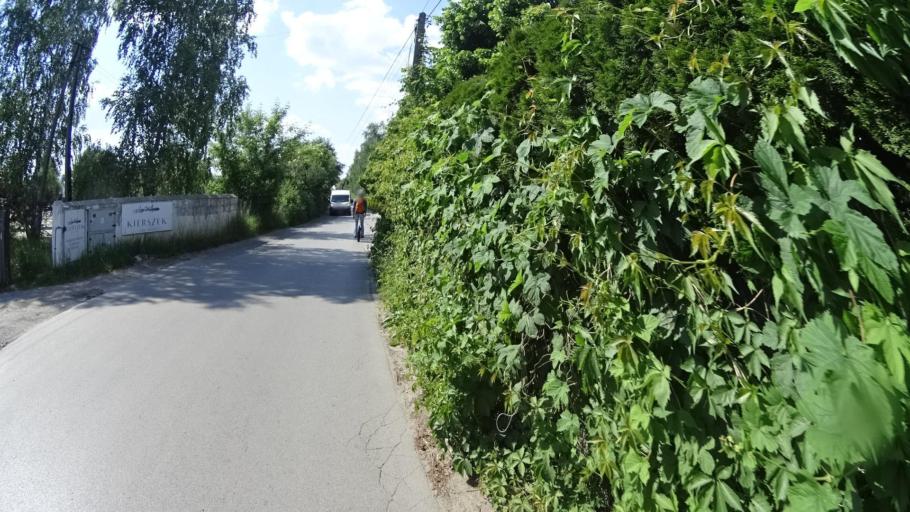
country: PL
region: Masovian Voivodeship
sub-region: Powiat piaseczynski
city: Jozefoslaw
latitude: 52.1047
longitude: 21.0582
